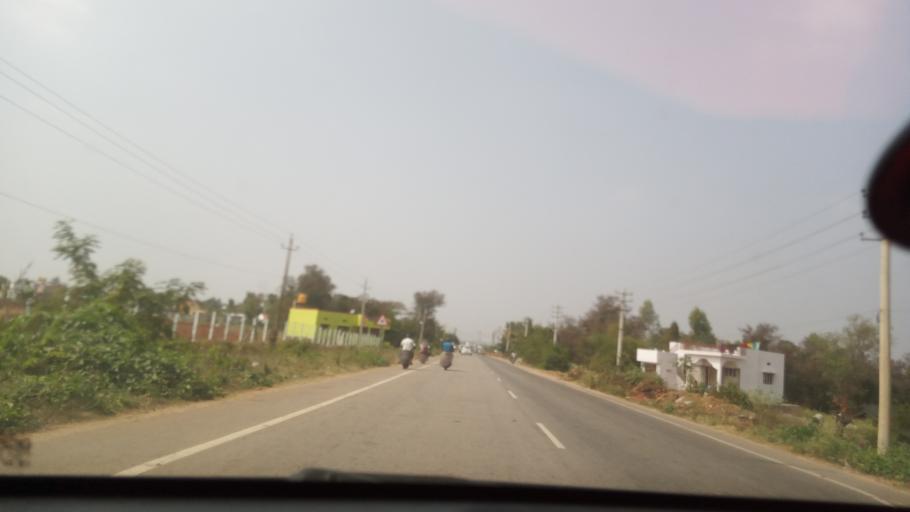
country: IN
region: Karnataka
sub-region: Chamrajnagar
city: Chamrajnagar
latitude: 11.9855
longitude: 76.8731
